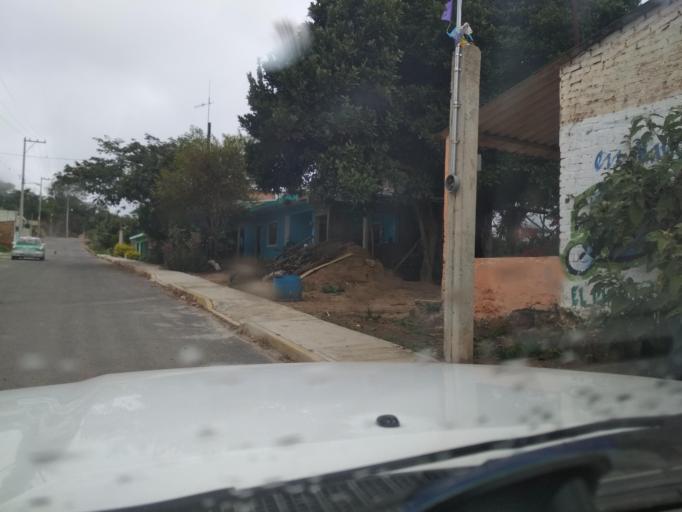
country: MX
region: Veracruz
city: El Castillo
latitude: 19.5398
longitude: -96.8237
